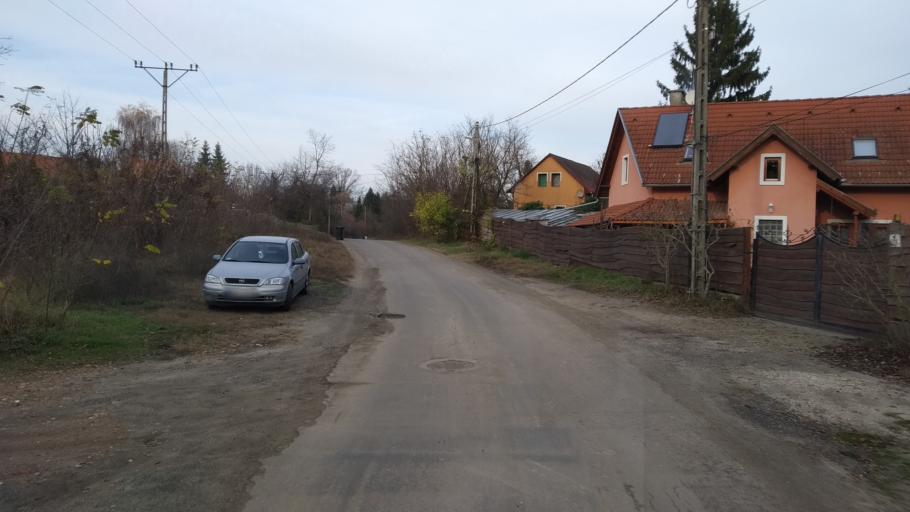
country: HU
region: Pest
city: God
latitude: 47.6733
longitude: 19.1111
